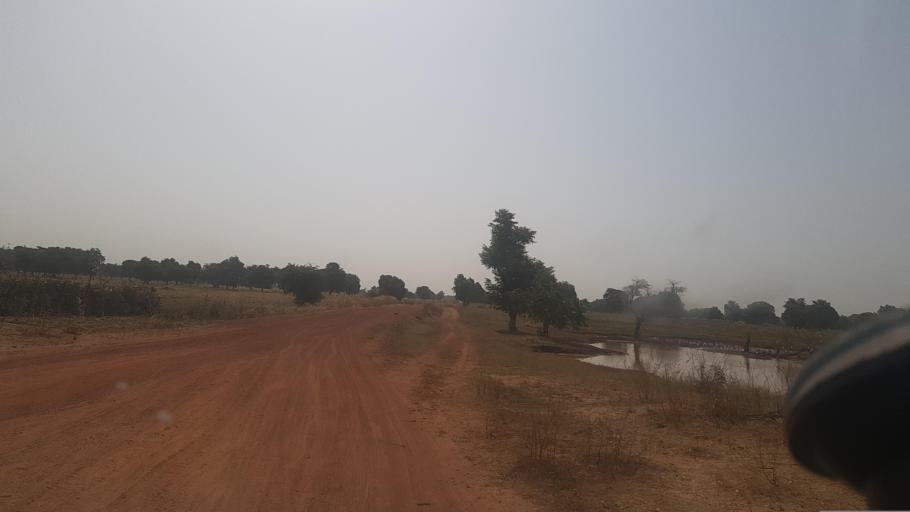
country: ML
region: Segou
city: Baroueli
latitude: 13.0067
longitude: -6.4206
